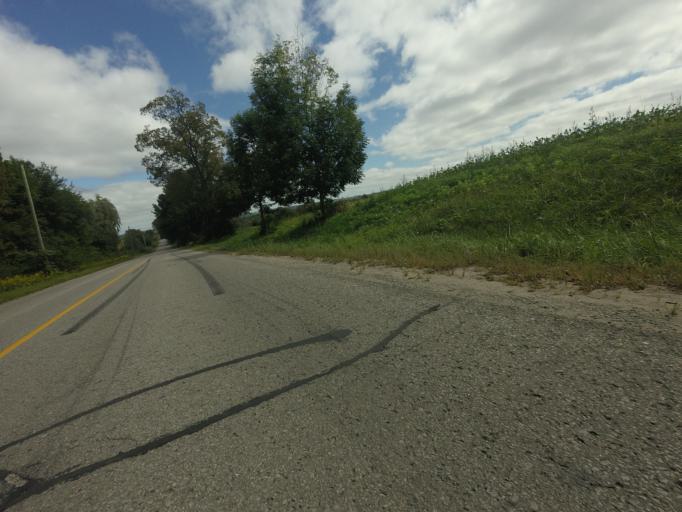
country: CA
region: Ontario
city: Uxbridge
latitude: 44.1241
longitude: -79.1398
